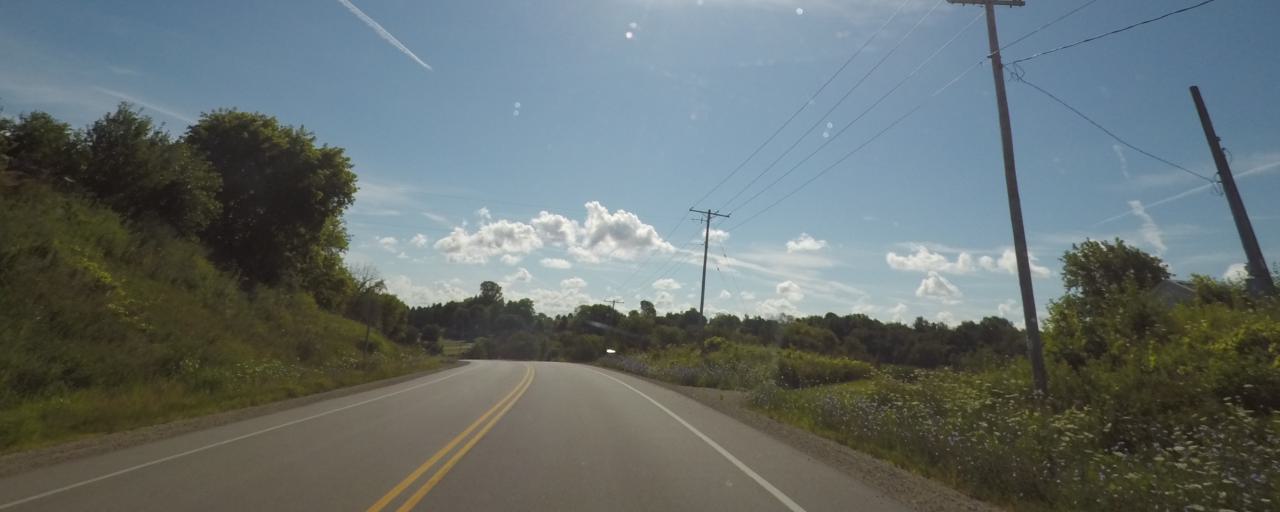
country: US
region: Wisconsin
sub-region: Jefferson County
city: Ixonia
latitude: 43.0725
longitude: -88.6463
